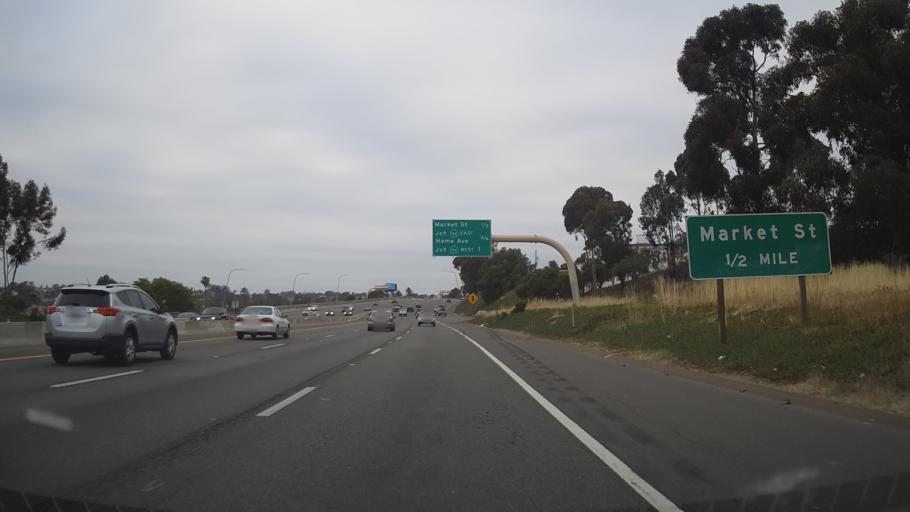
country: US
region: California
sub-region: San Diego County
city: National City
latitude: 32.7021
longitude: -117.1206
